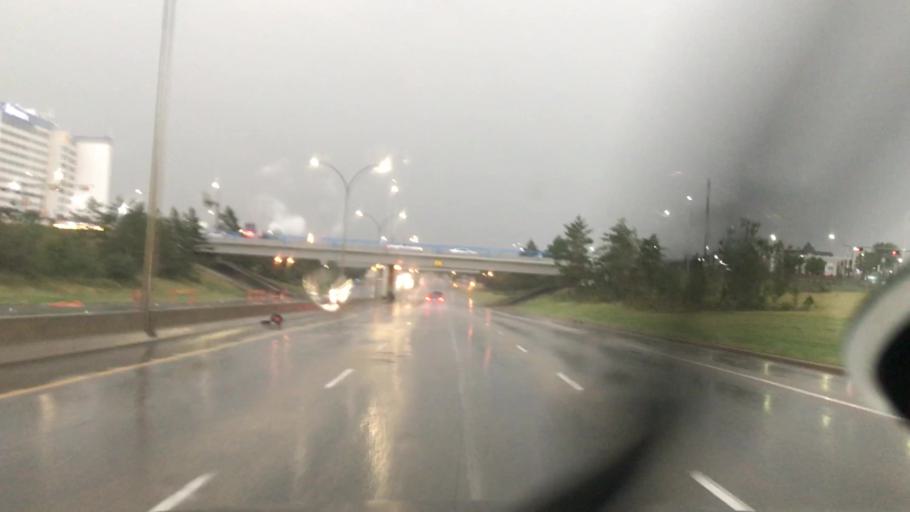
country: CA
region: Alberta
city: Edmonton
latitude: 53.4803
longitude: -113.4974
